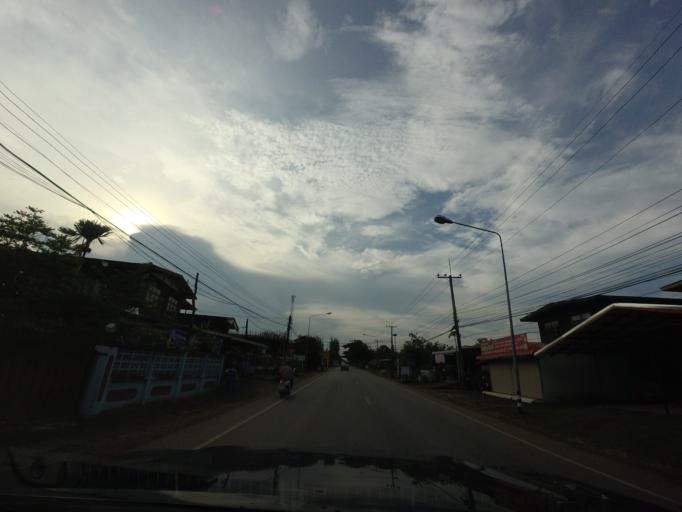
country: TH
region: Changwat Udon Thani
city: Nam Som
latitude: 17.8022
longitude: 102.2789
